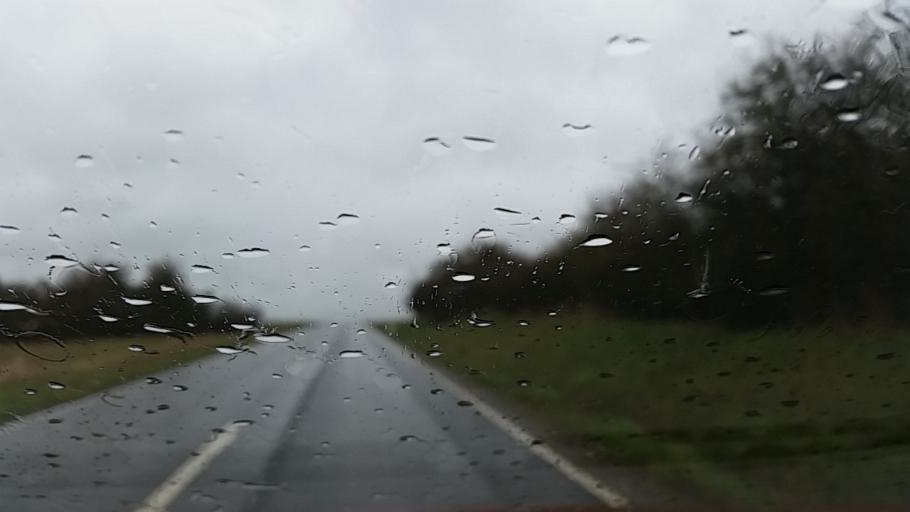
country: DE
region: Bavaria
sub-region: Regierungsbezirk Unterfranken
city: Marktheidenfeld
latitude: 49.8545
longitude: 9.6167
